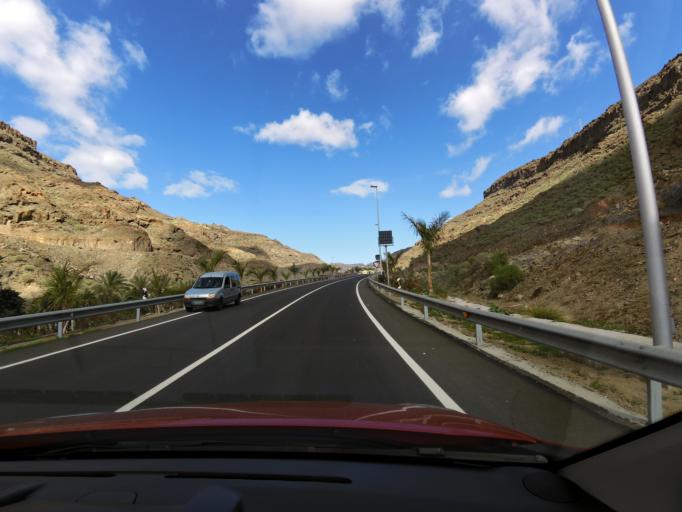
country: ES
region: Canary Islands
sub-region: Provincia de Las Palmas
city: Puerto Rico
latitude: 27.8223
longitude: -15.7488
